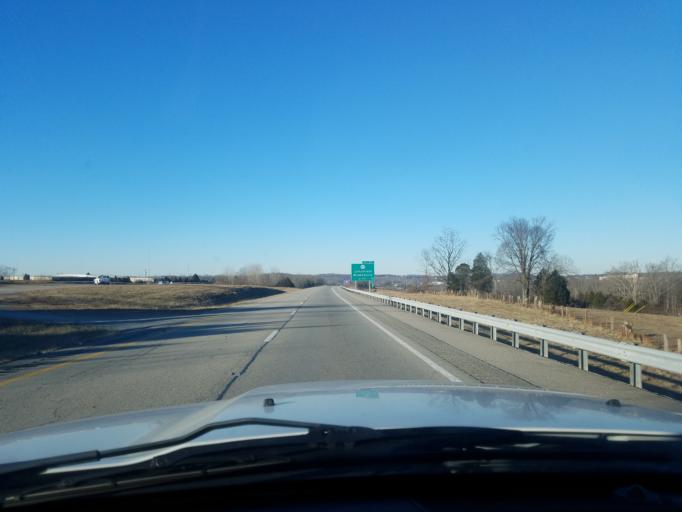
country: US
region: Kentucky
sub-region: Grayson County
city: Leitchfield
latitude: 37.4684
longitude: -86.2730
